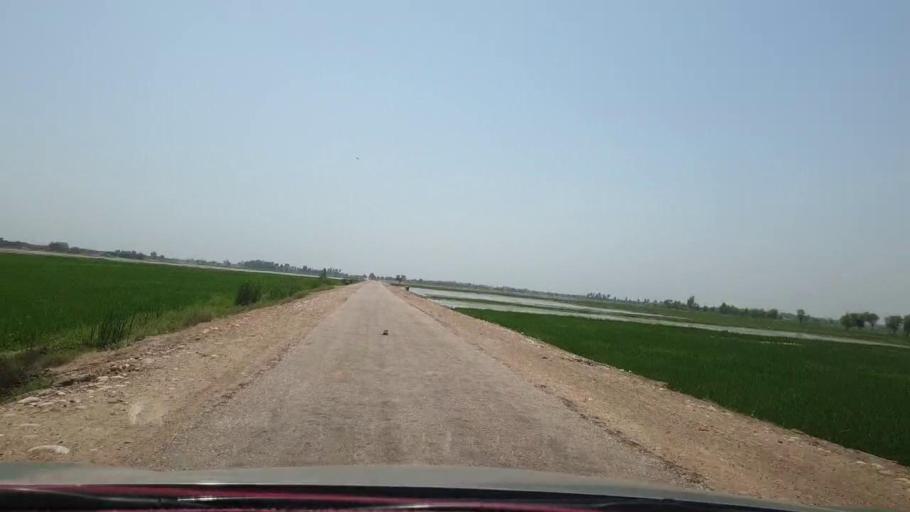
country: PK
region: Sindh
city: Warah
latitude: 27.5521
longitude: 67.7963
